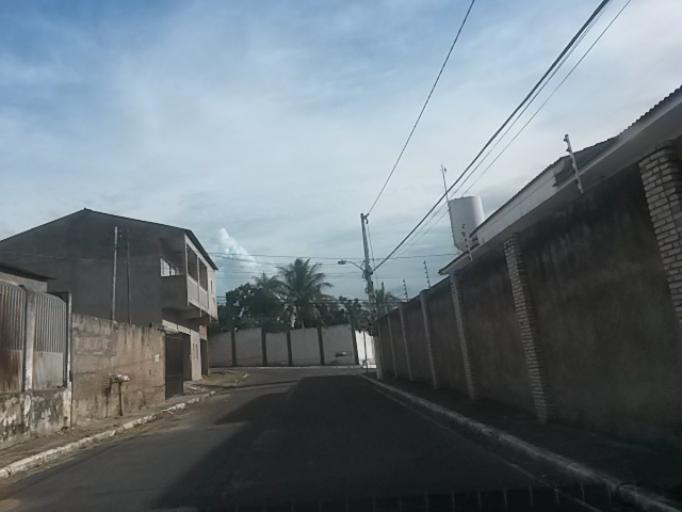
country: BR
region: Mato Grosso
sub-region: Cuiaba
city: Cuiaba
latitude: -15.6005
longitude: -56.0791
